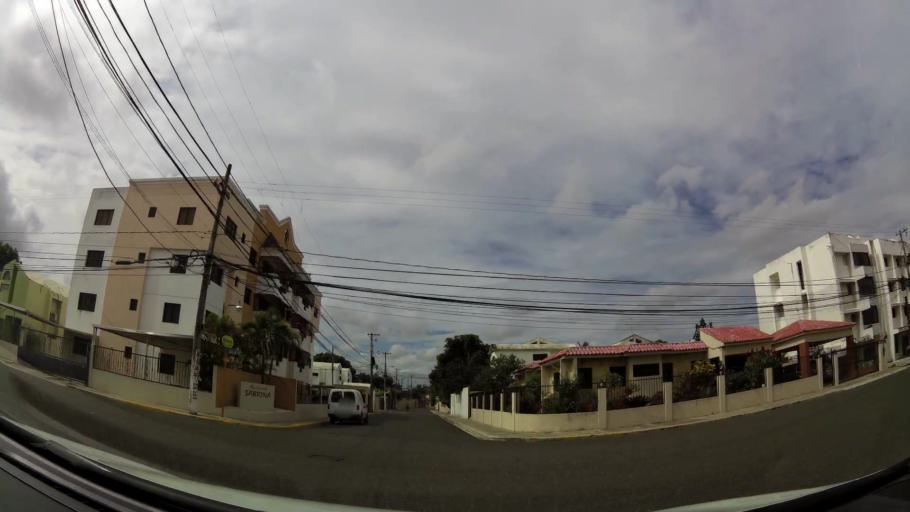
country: DO
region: Santiago
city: Santiago de los Caballeros
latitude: 19.4424
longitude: -70.6718
